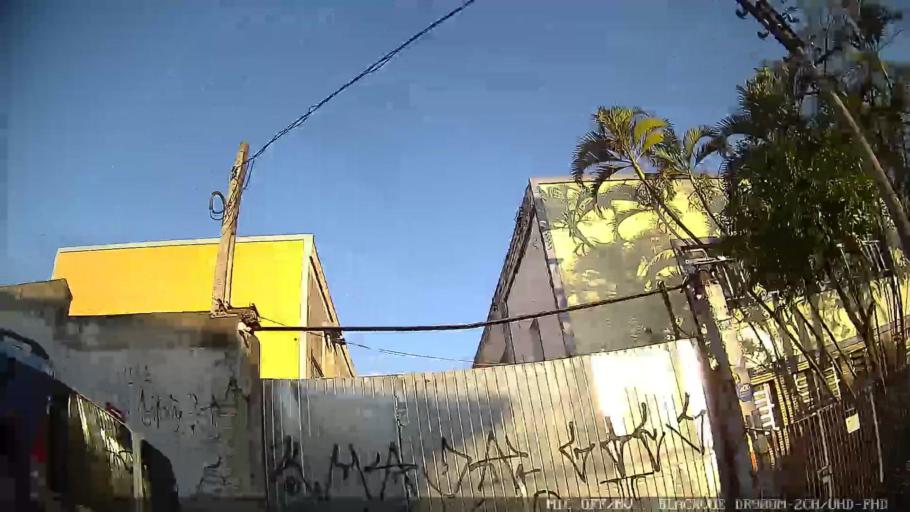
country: BR
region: Sao Paulo
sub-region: Sao Caetano Do Sul
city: Sao Caetano do Sul
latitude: -23.5801
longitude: -46.5497
